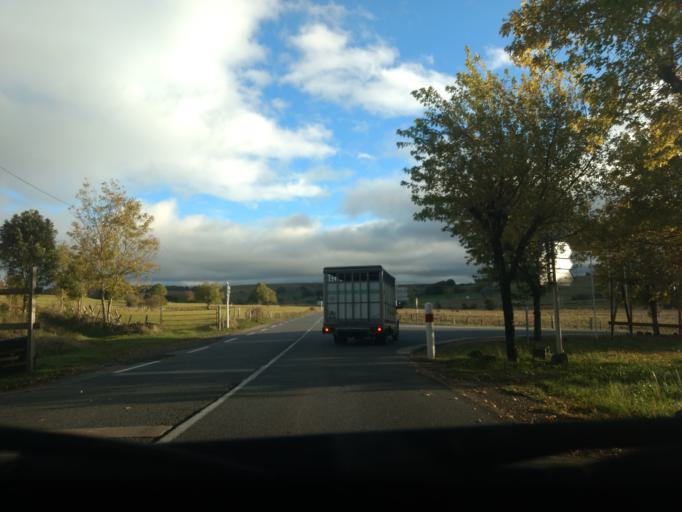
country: FR
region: Midi-Pyrenees
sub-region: Departement de l'Aveyron
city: Laguiole
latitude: 44.7652
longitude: 2.8828
